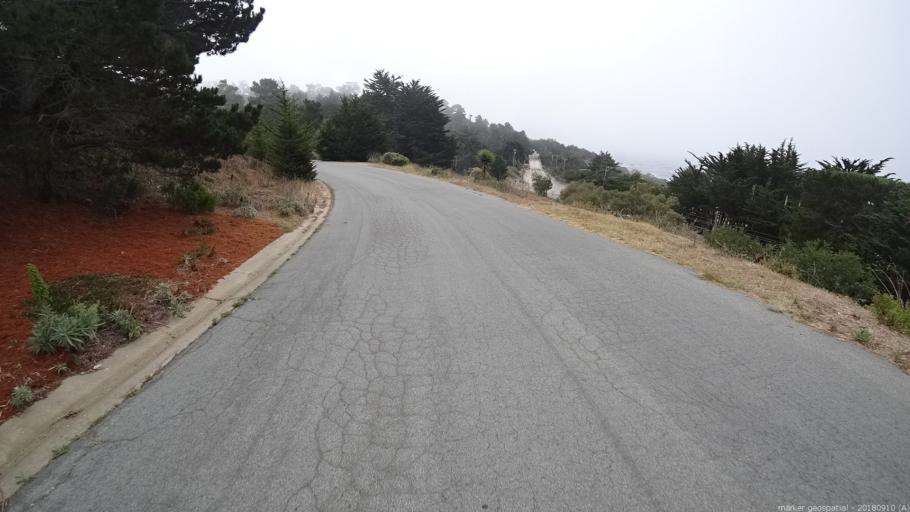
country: US
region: California
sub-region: Monterey County
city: Carmel-by-the-Sea
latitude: 36.4842
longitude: -121.9369
